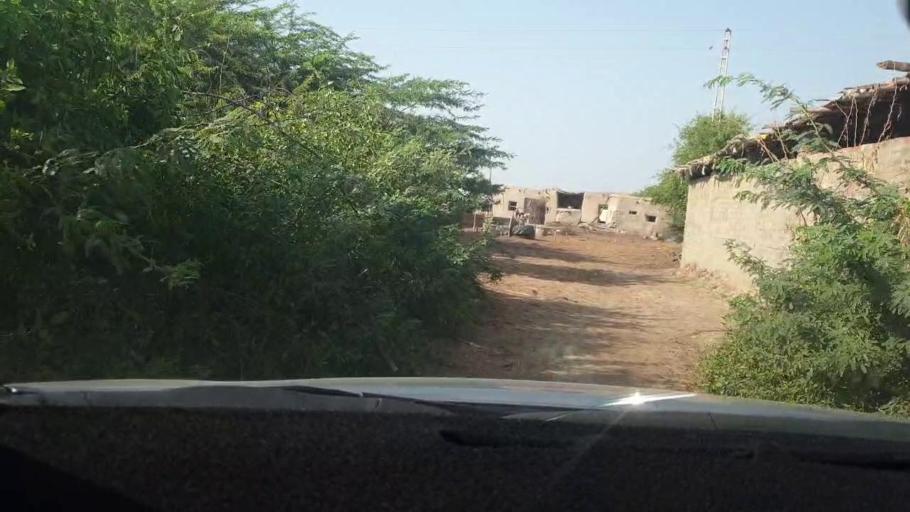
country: PK
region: Sindh
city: Pithoro
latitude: 25.7944
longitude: 69.4124
